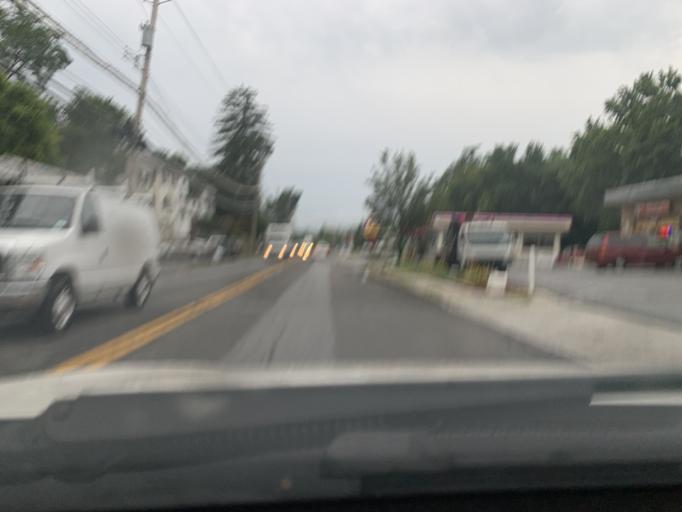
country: US
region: New York
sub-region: Westchester County
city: Ossining
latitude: 41.1729
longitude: -73.8661
